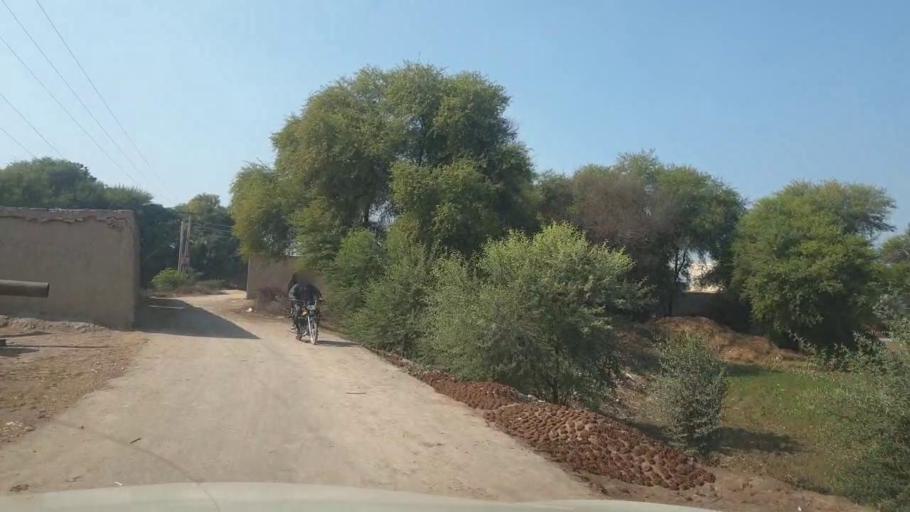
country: PK
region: Sindh
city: Bhan
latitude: 26.5840
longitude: 67.6993
